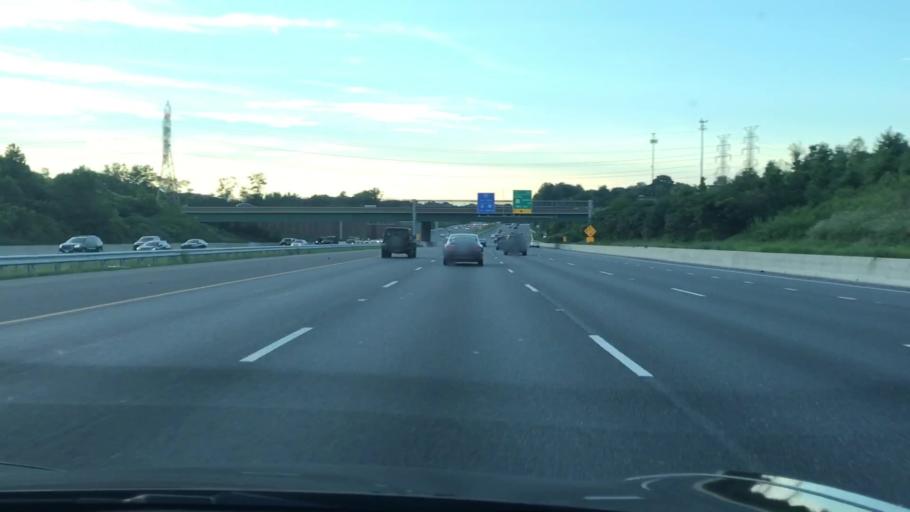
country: US
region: Maryland
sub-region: Baltimore County
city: Overlea
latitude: 39.3597
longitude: -76.5042
